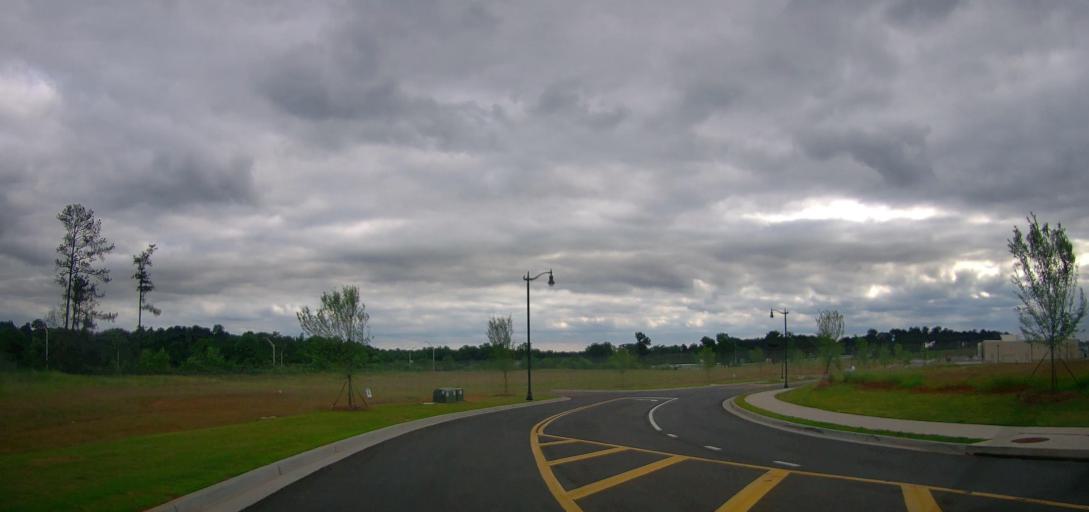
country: US
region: Georgia
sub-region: Walton County
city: Monroe
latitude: 33.8069
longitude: -83.7257
